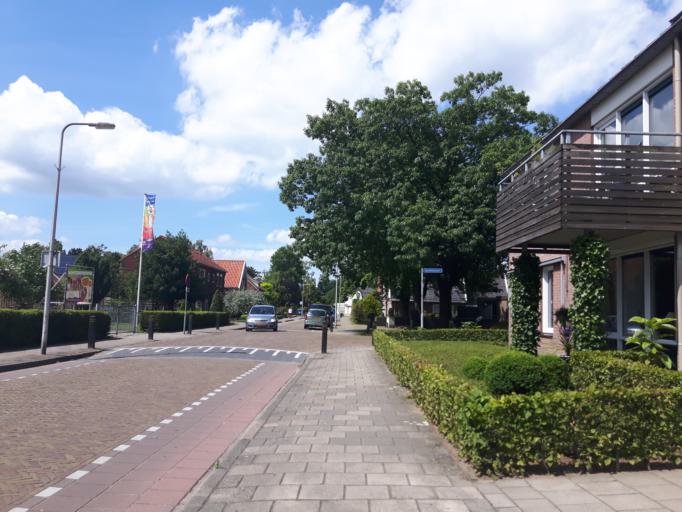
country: NL
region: Overijssel
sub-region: Gemeente Haaksbergen
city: Haaksbergen
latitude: 52.1649
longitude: 6.7545
